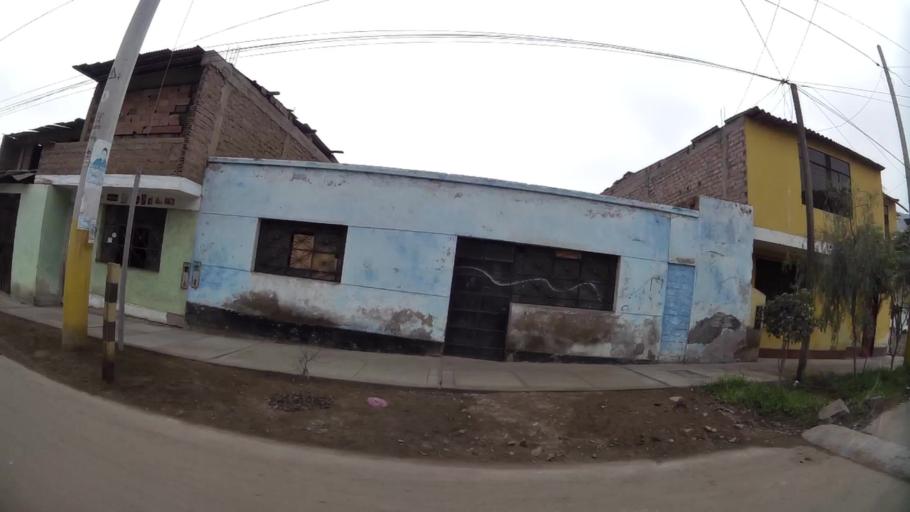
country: PE
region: Lima
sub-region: Lima
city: Surco
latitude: -12.2083
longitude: -76.9098
